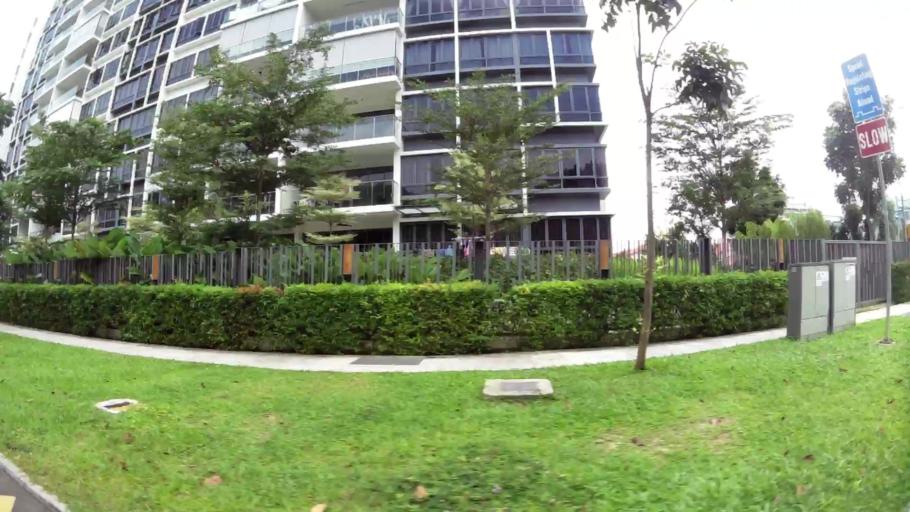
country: SG
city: Singapore
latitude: 1.3389
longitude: 103.9271
